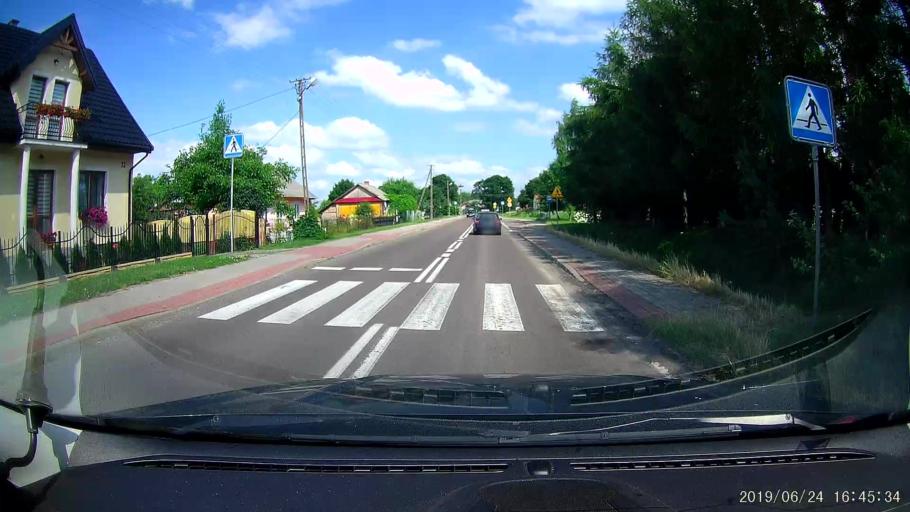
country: PL
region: Lublin Voivodeship
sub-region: Powiat tomaszowski
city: Laszczow
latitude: 50.5321
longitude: 23.6700
